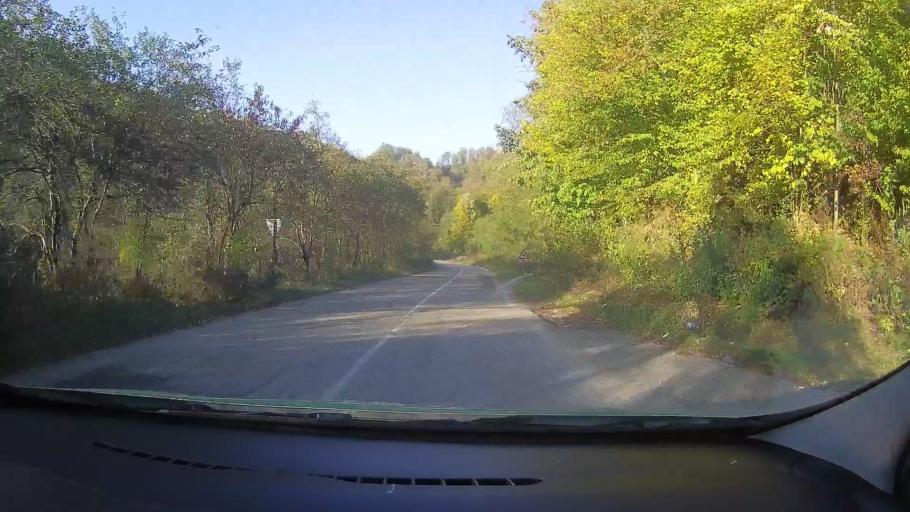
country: RO
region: Timis
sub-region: Comuna Nadrag
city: Nadrag
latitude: 45.6680
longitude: 22.1647
